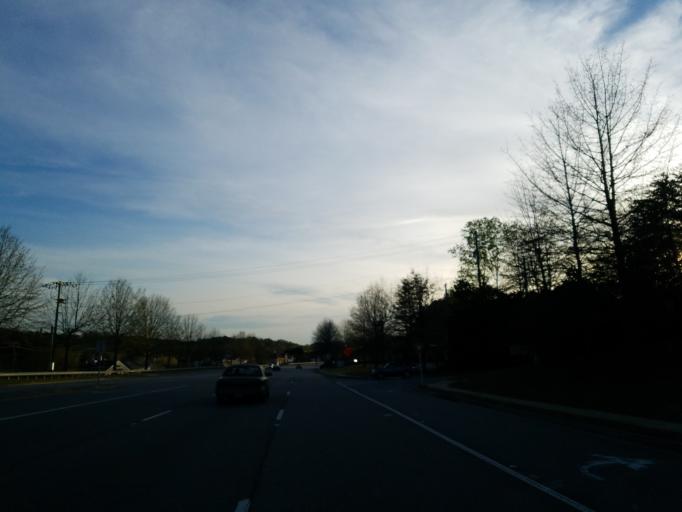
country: US
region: Georgia
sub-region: Cherokee County
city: Canton
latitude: 34.2474
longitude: -84.4796
